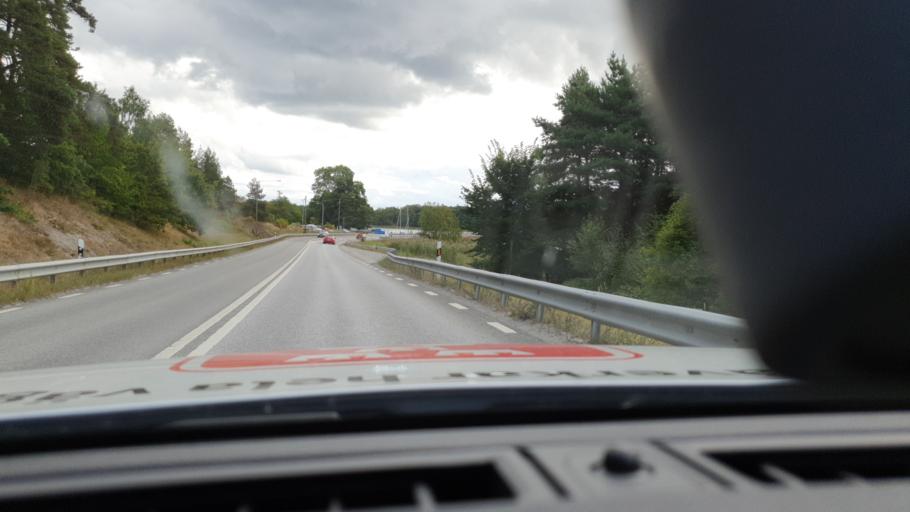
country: SE
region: Stockholm
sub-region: Vaxholms Kommun
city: Resaro
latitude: 59.4180
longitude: 18.3060
